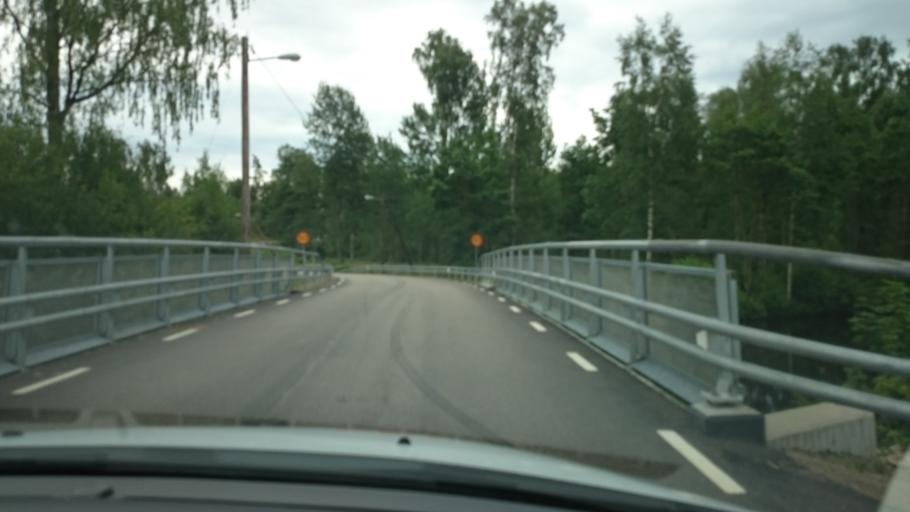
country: SE
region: Halland
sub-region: Hylte Kommun
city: Torup
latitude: 56.9598
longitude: 13.1549
